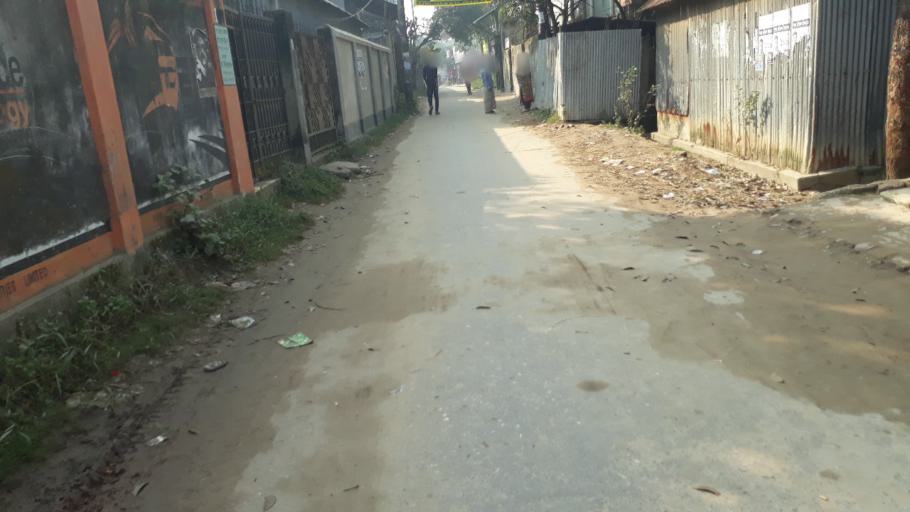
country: BD
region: Dhaka
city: Tungi
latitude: 23.8861
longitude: 90.2621
